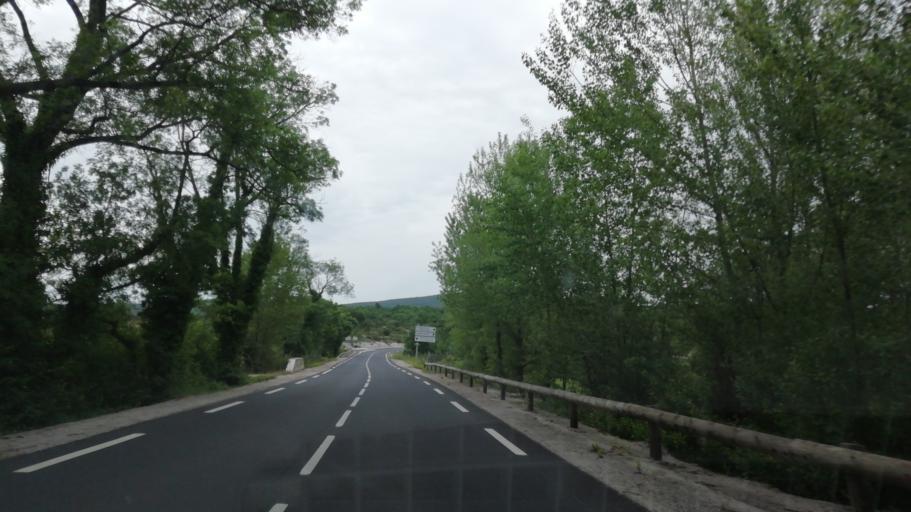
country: FR
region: Languedoc-Roussillon
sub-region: Departement de l'Herault
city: Saint-Mathieu-de-Treviers
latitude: 43.7934
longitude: 3.7988
